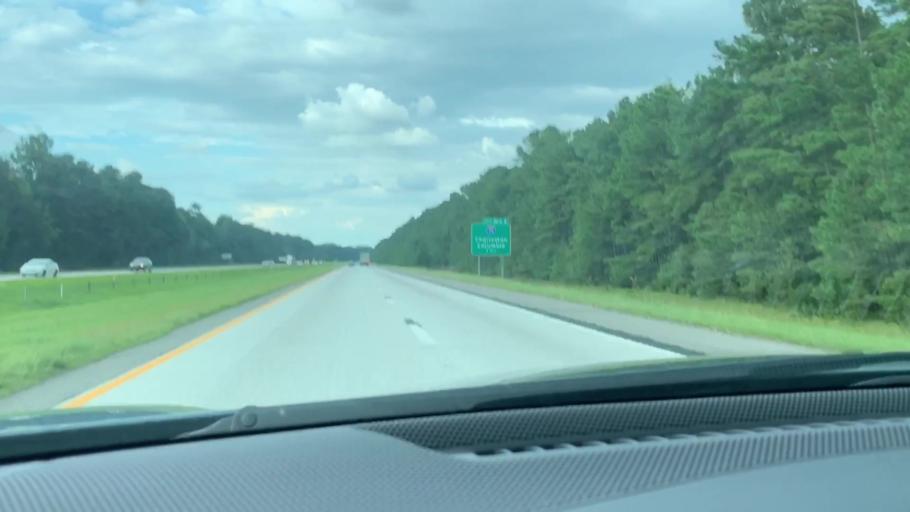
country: US
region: South Carolina
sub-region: Dorchester County
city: Saint George
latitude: 33.3001
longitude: -80.5561
